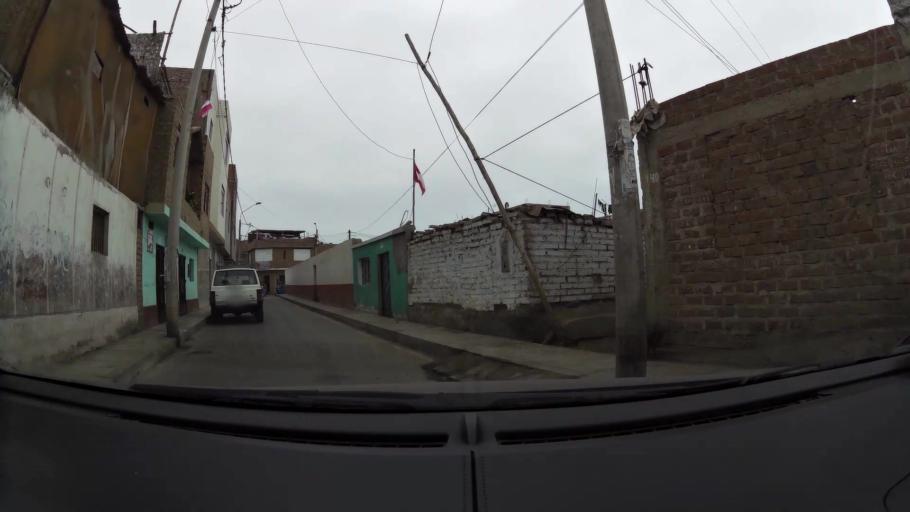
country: PE
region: Lima
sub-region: Barranca
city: Barranca
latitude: -10.7466
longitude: -77.7589
